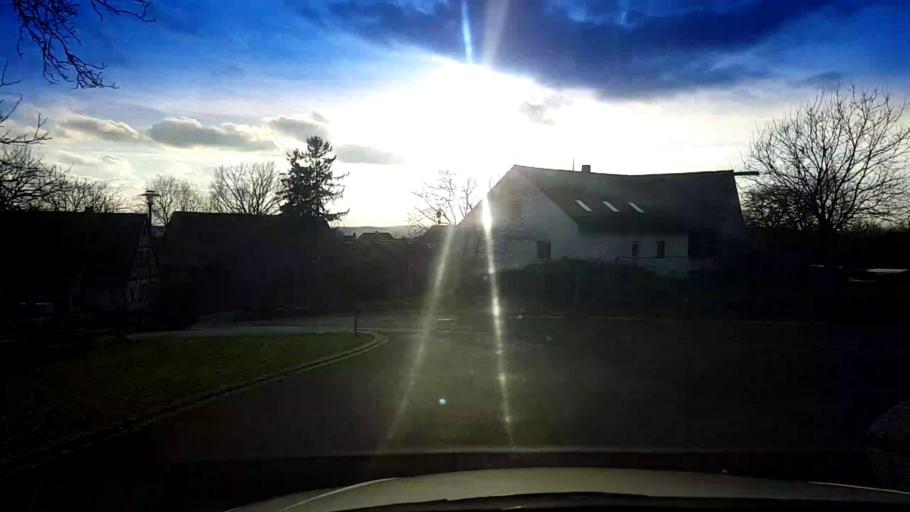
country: DE
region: Bavaria
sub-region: Upper Franconia
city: Buttenheim
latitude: 49.8384
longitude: 11.0341
